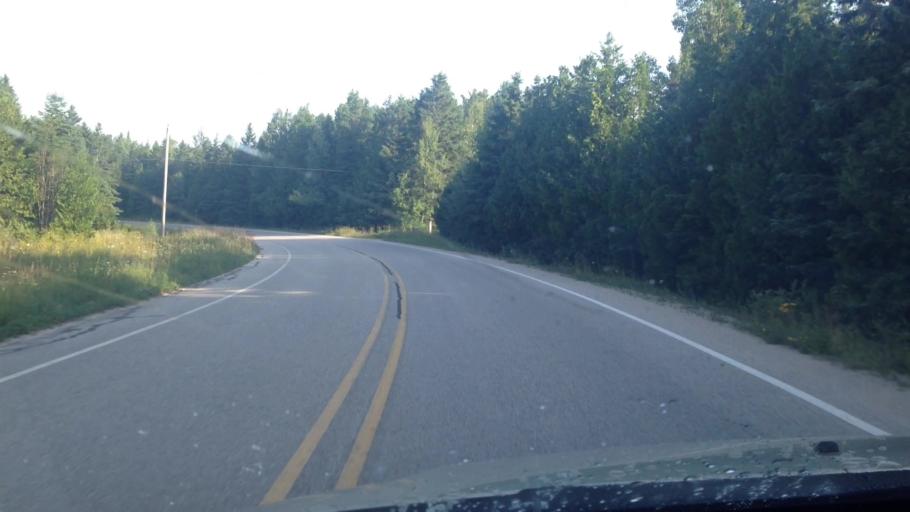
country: US
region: Michigan
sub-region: Mackinac County
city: Saint Ignace
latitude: 45.8920
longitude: -84.7662
